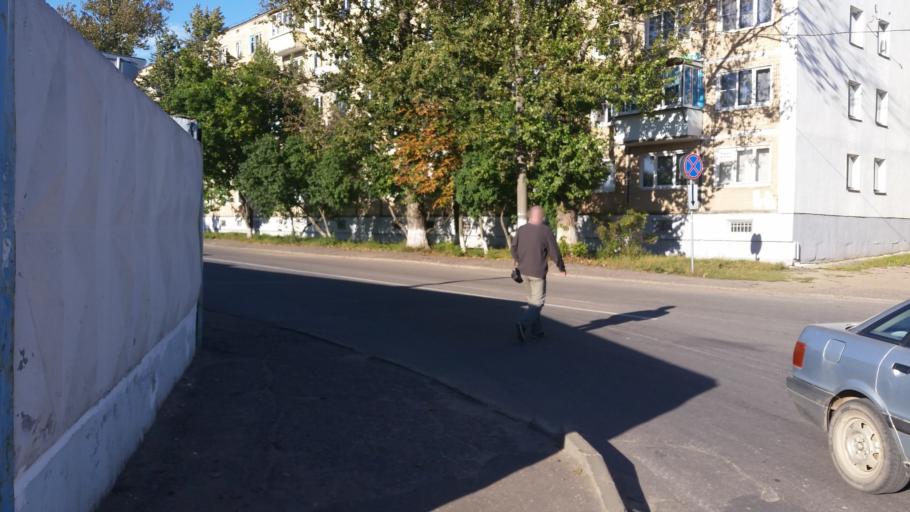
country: BY
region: Vitebsk
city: Vitebsk
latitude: 55.1782
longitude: 30.1873
